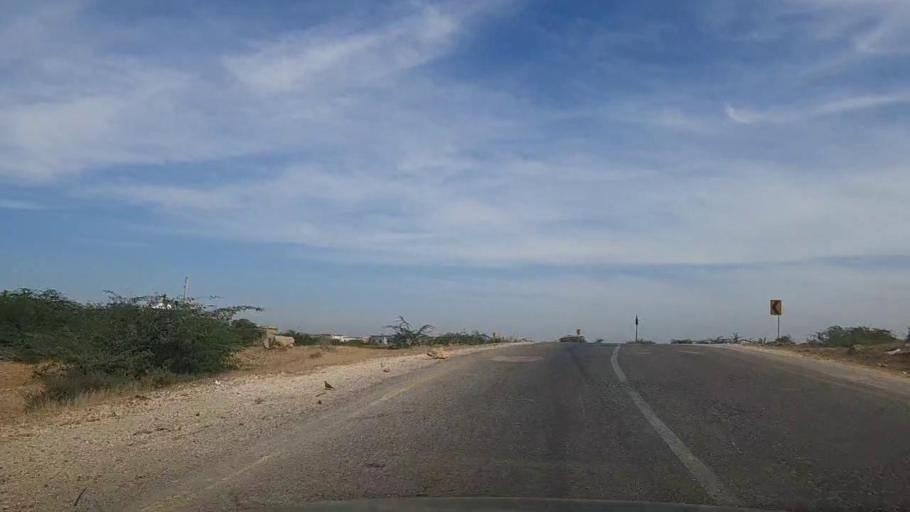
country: PK
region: Sindh
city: Daro Mehar
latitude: 24.9116
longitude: 68.0732
